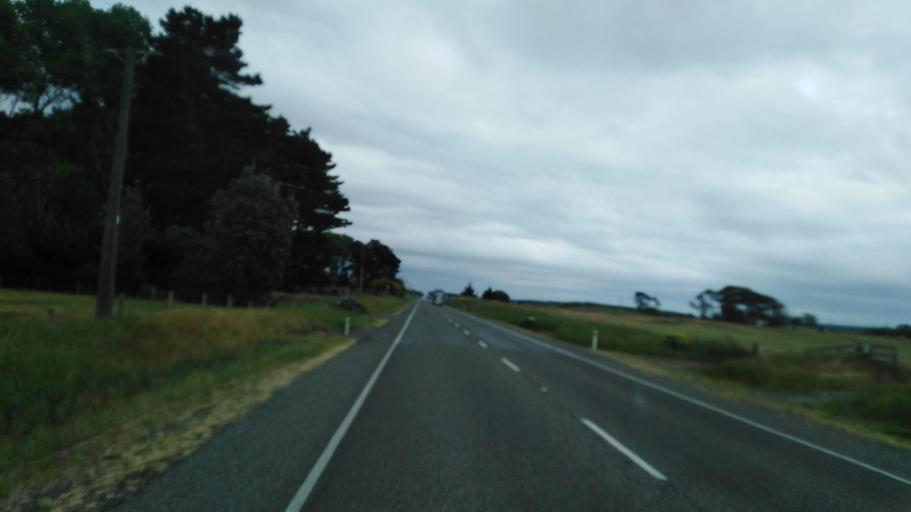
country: NZ
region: Manawatu-Wanganui
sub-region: Horowhenua District
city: Foxton
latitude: -40.3854
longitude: 175.3171
